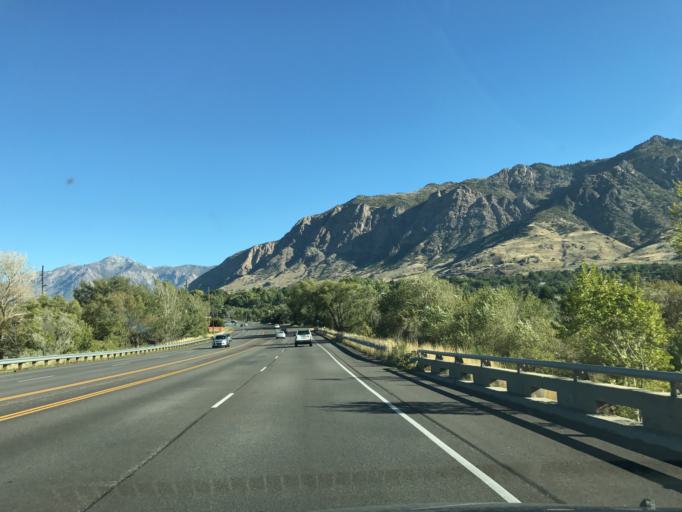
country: US
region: Utah
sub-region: Weber County
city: Ogden
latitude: 41.2367
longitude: -111.9461
